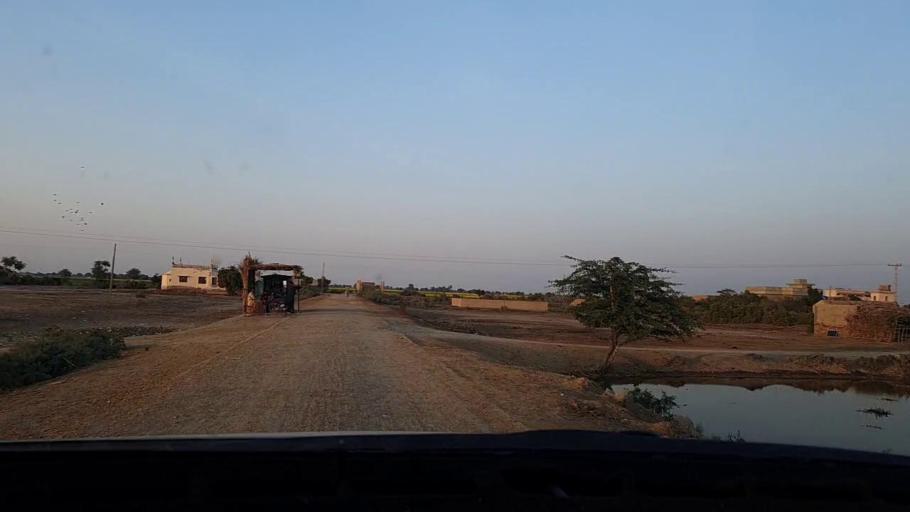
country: PK
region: Sindh
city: Tando Mittha Khan
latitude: 25.8515
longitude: 69.2305
